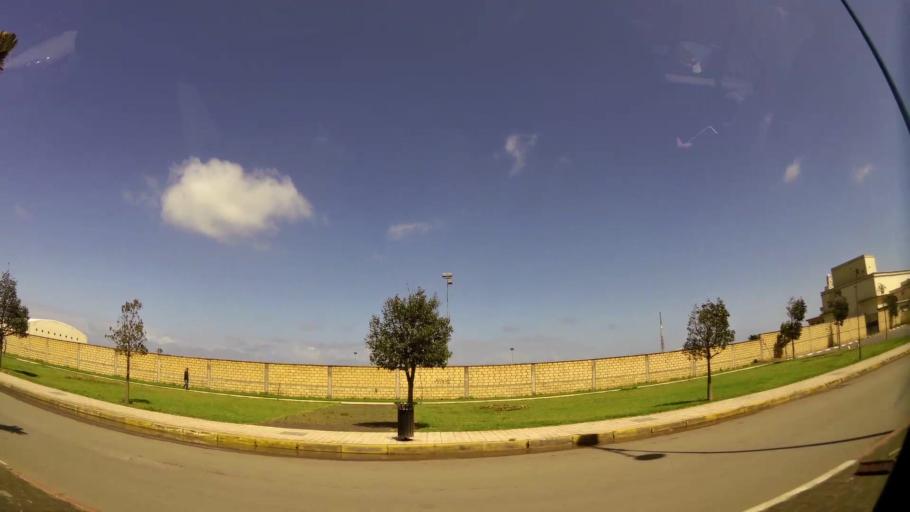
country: MA
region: Grand Casablanca
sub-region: Mediouna
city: Tit Mellil
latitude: 33.6339
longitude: -7.4565
